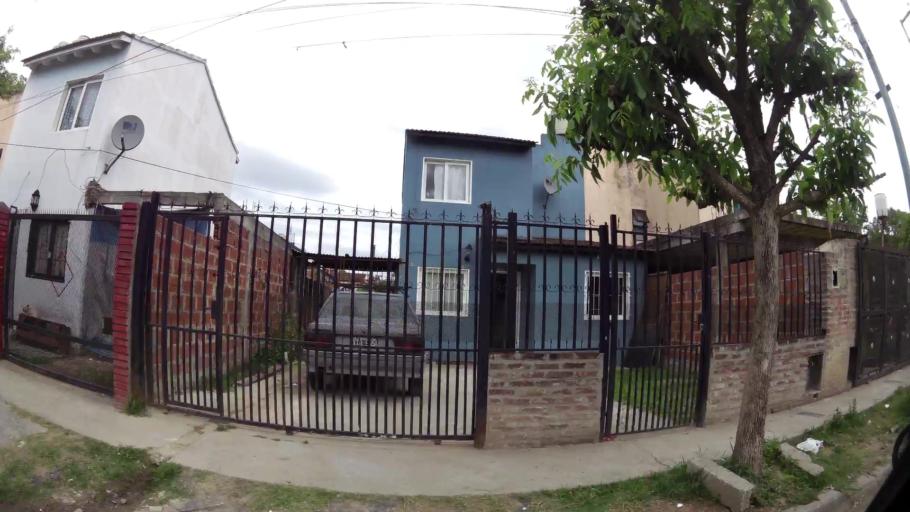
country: AR
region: Buenos Aires
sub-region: Partido de Quilmes
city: Quilmes
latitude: -34.7514
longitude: -58.2508
